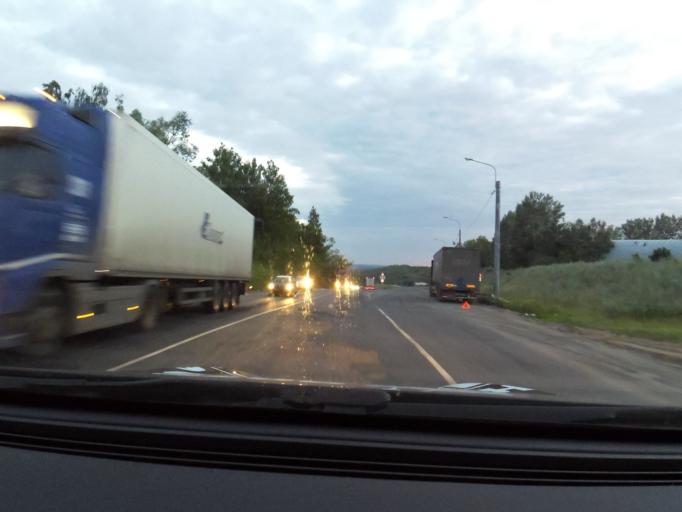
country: RU
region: Chuvashia
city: Yadrin
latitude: 56.0391
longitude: 46.2722
